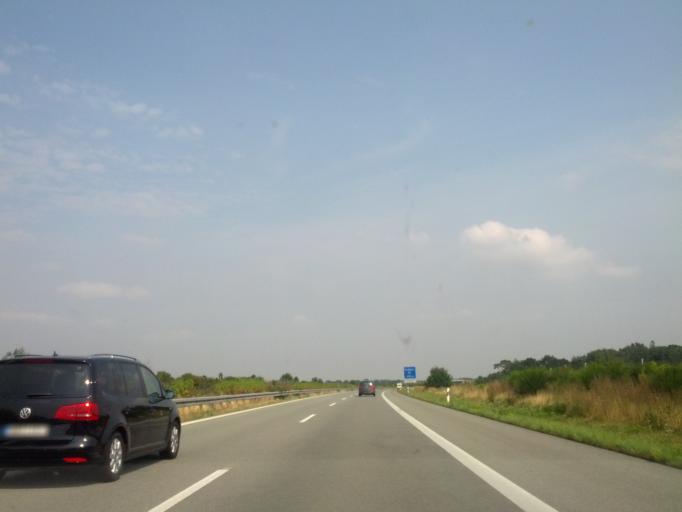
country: DE
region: Mecklenburg-Vorpommern
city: Bad Sulze
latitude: 54.0474
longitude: 12.6164
